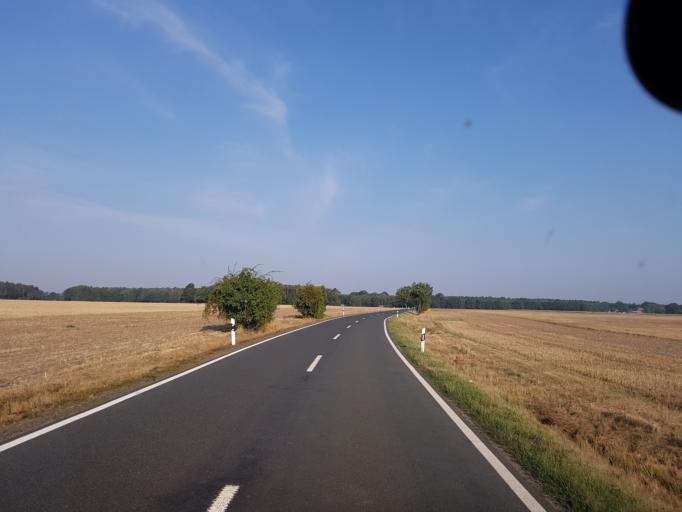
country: DE
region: Brandenburg
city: Finsterwalde
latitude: 51.6744
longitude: 13.7030
